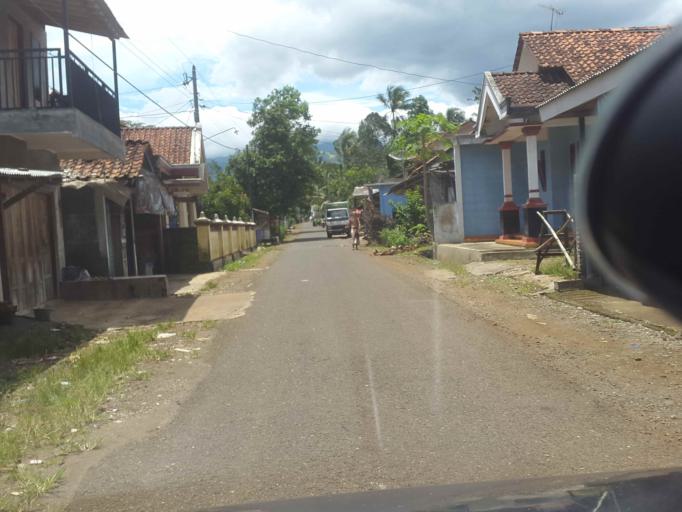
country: ID
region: Central Java
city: Tipar
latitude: -7.4183
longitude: 109.1278
